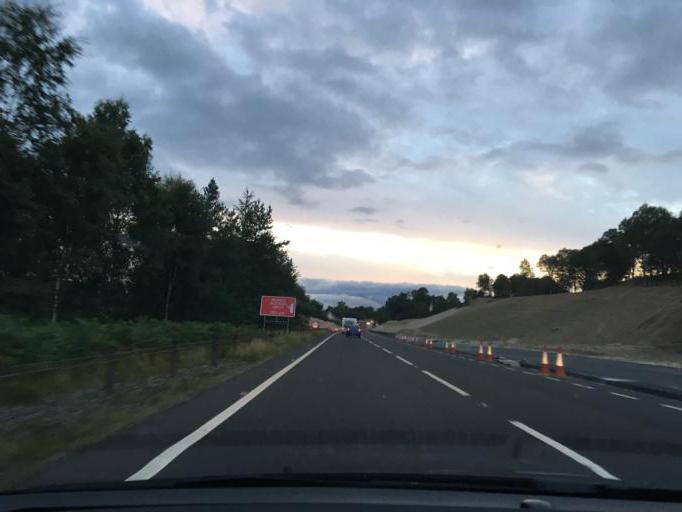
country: GB
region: Scotland
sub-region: Highland
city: Kingussie
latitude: 57.1113
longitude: -3.9589
